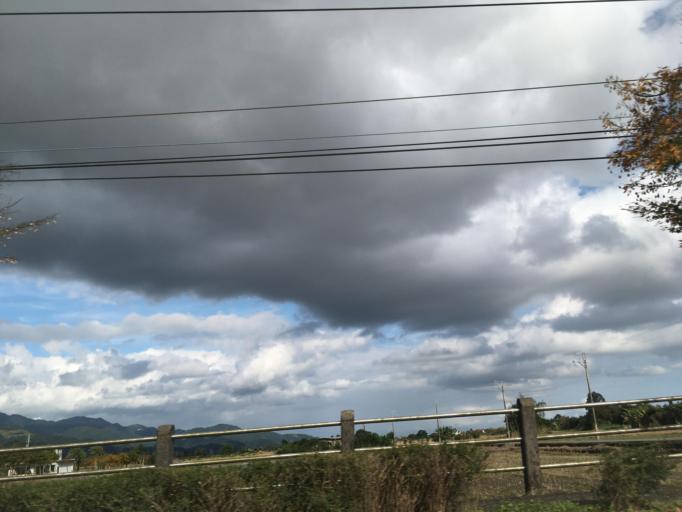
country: TW
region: Taiwan
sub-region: Yilan
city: Yilan
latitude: 24.6653
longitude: 121.6172
